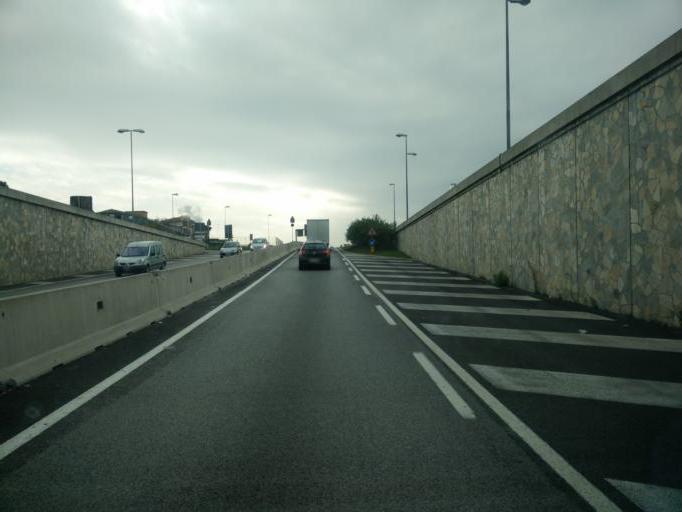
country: IT
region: Tuscany
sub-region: Provincia di Prato
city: Prato
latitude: 43.8728
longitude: 11.0825
